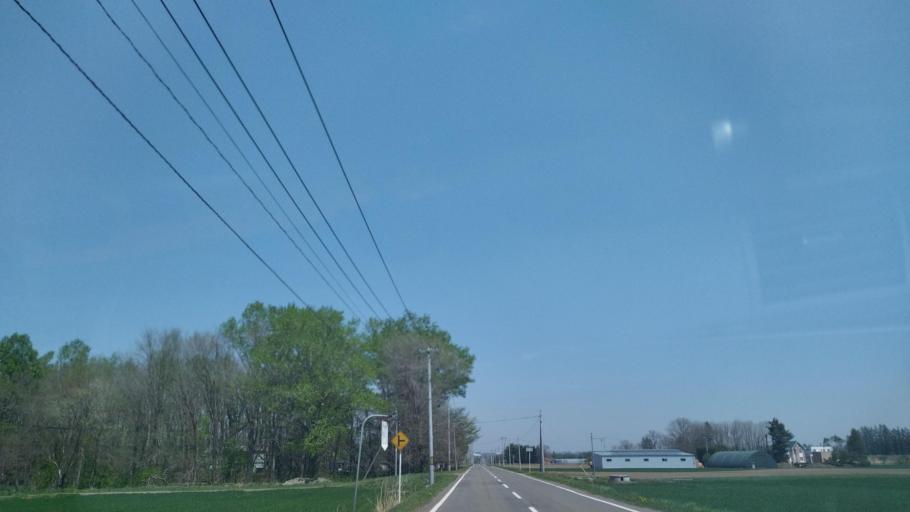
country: JP
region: Hokkaido
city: Obihiro
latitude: 42.8848
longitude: 143.0217
